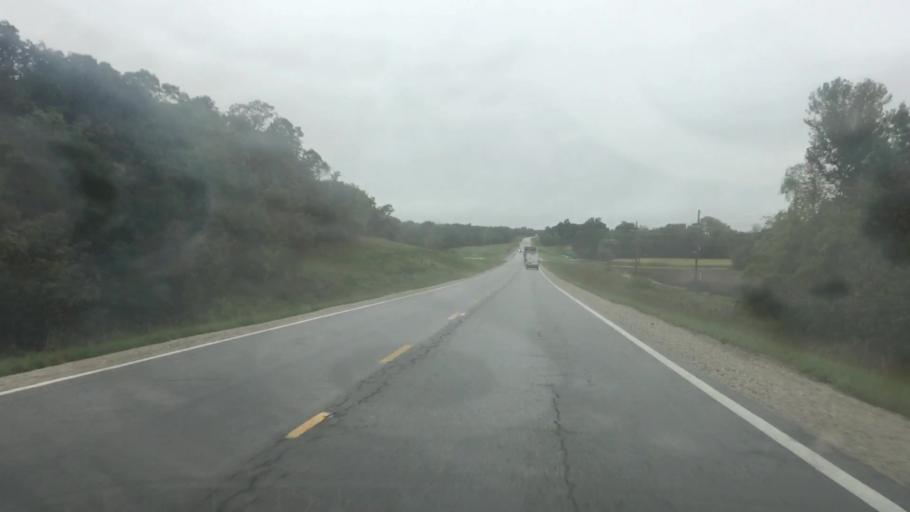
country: US
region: Kansas
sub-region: Anderson County
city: Garnett
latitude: 38.2151
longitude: -95.2488
